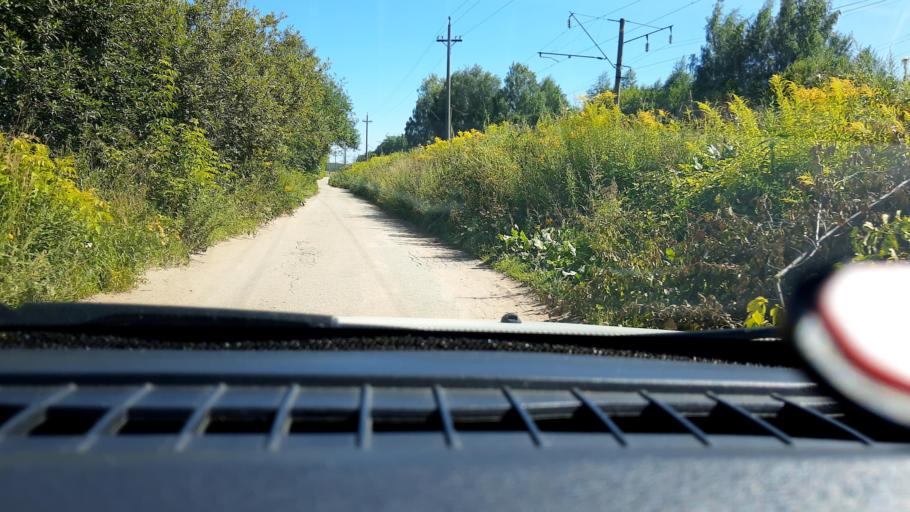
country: RU
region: Nizjnij Novgorod
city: Afonino
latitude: 56.2377
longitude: 44.0411
